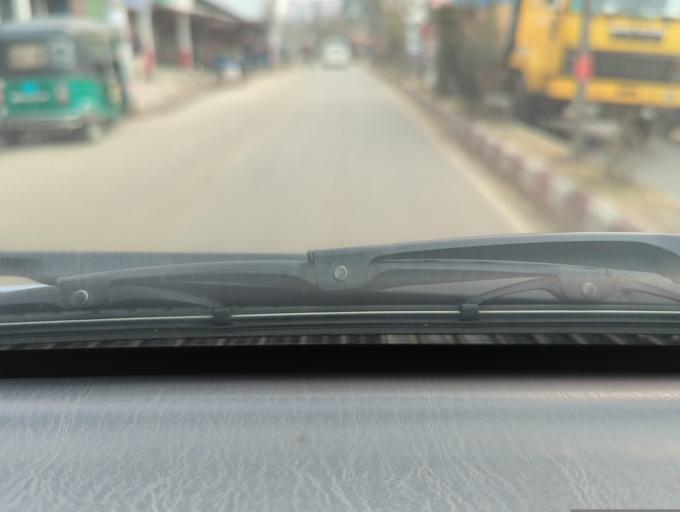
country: BD
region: Sylhet
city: Maulavi Bazar
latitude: 24.4874
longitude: 91.7642
